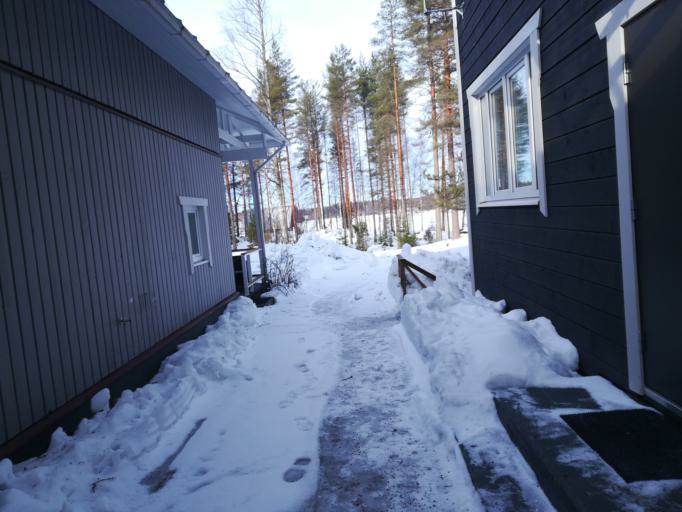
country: FI
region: Southern Savonia
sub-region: Savonlinna
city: Savonlinna
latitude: 61.8292
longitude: 29.0238
